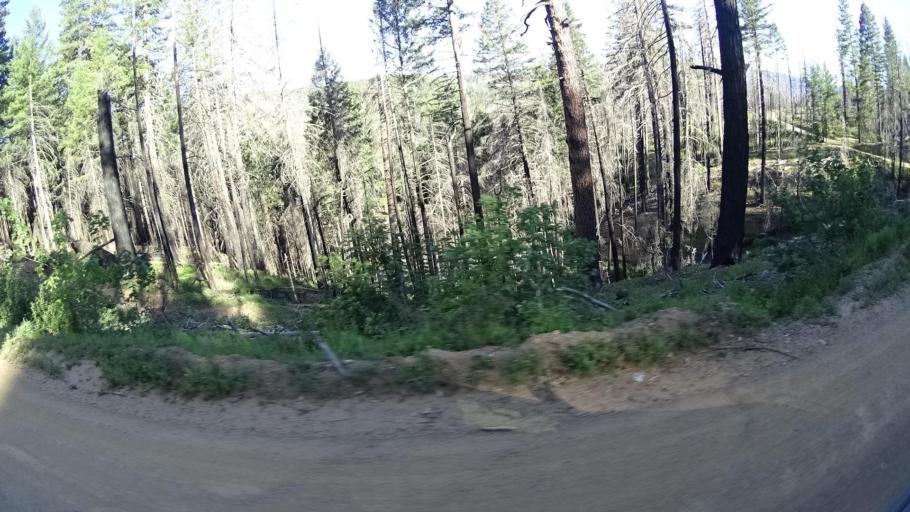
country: US
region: California
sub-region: Lake County
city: Upper Lake
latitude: 39.3673
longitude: -122.9920
